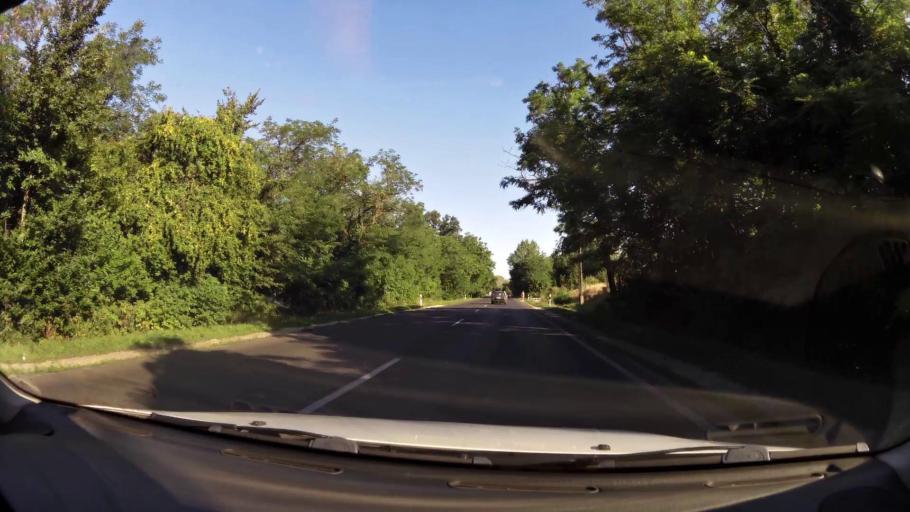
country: HU
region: Pest
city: Nyaregyhaza
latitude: 47.3124
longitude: 19.4955
